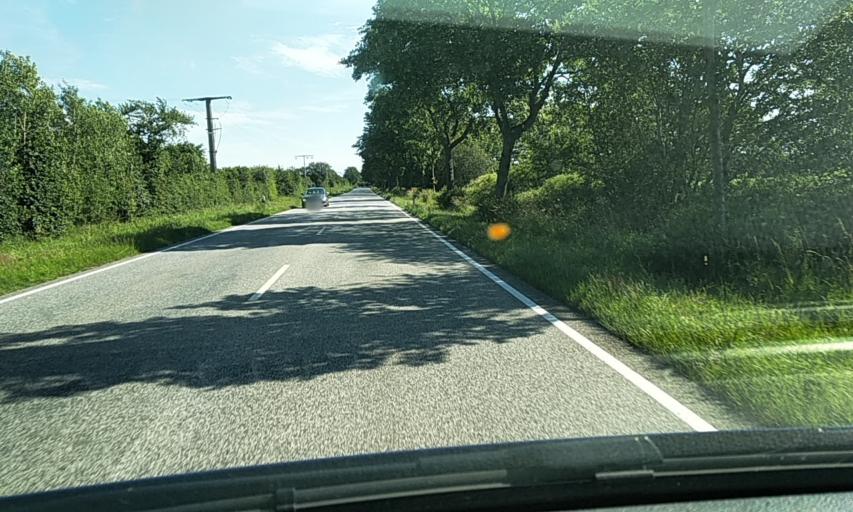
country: DE
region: Schleswig-Holstein
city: Fockbek
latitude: 54.2924
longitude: 9.5836
